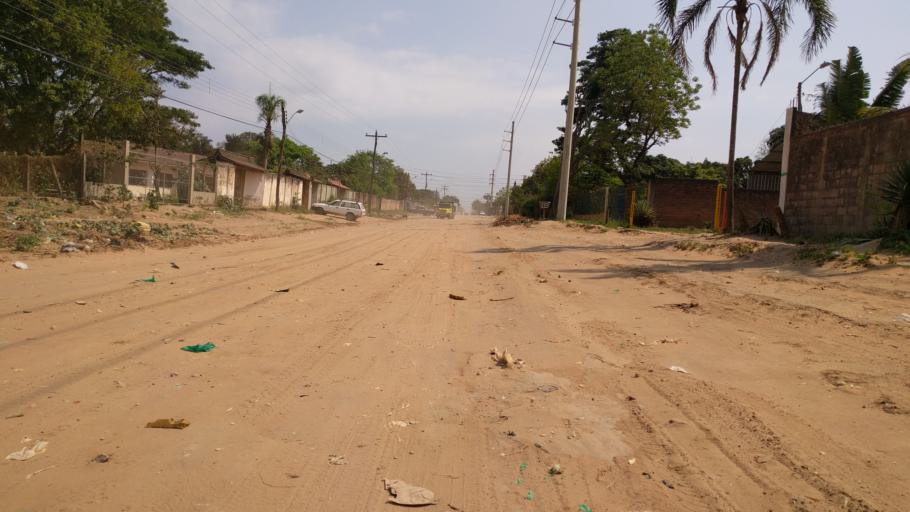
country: BO
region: Santa Cruz
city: Santa Cruz de la Sierra
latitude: -17.8529
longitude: -63.2174
